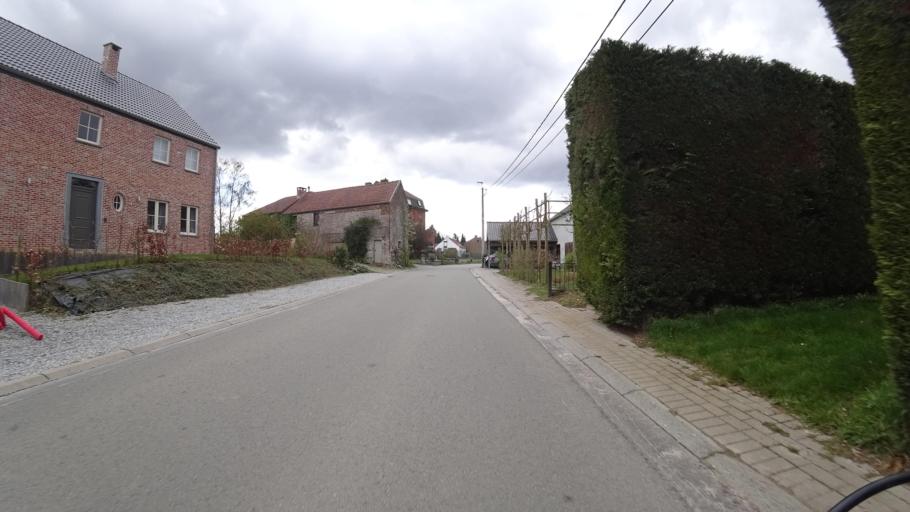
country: BE
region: Wallonia
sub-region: Province du Brabant Wallon
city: Walhain-Saint-Paul
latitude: 50.6290
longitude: 4.7250
